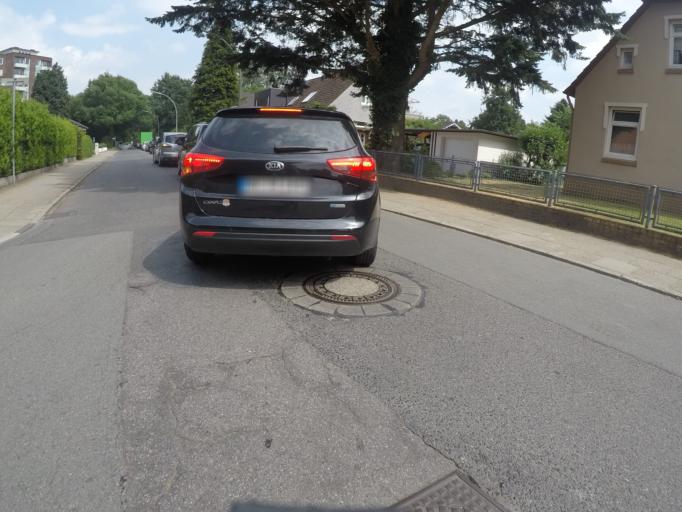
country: DE
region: Hamburg
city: Farmsen-Berne
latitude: 53.5905
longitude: 10.1402
